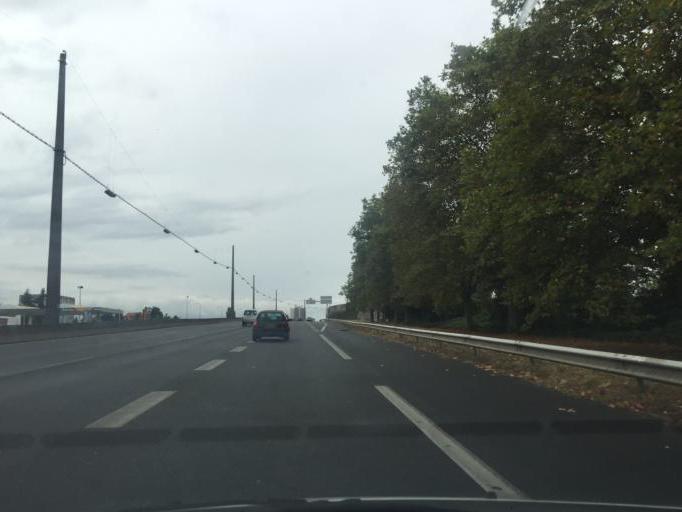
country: FR
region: Rhone-Alpes
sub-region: Departement du Rhone
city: Bron
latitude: 45.7406
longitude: 4.9048
